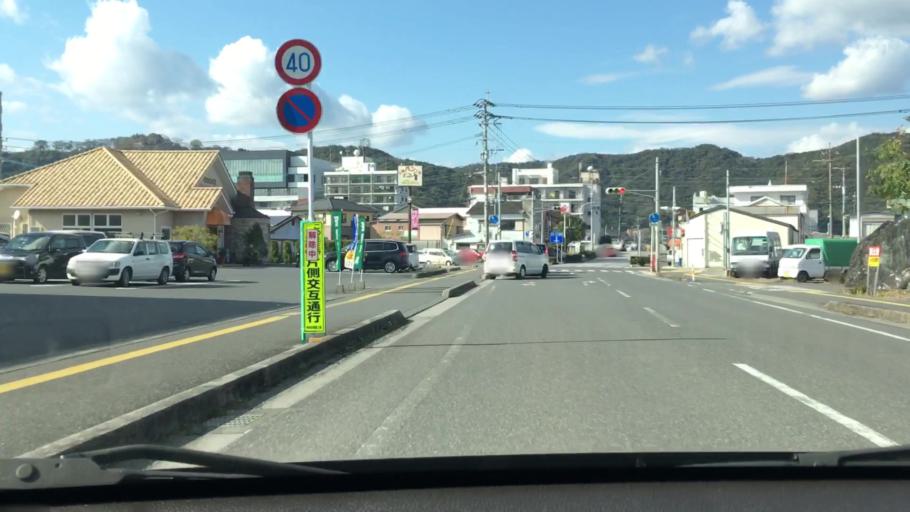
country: JP
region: Oita
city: Saiki
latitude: 32.9593
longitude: 131.9033
